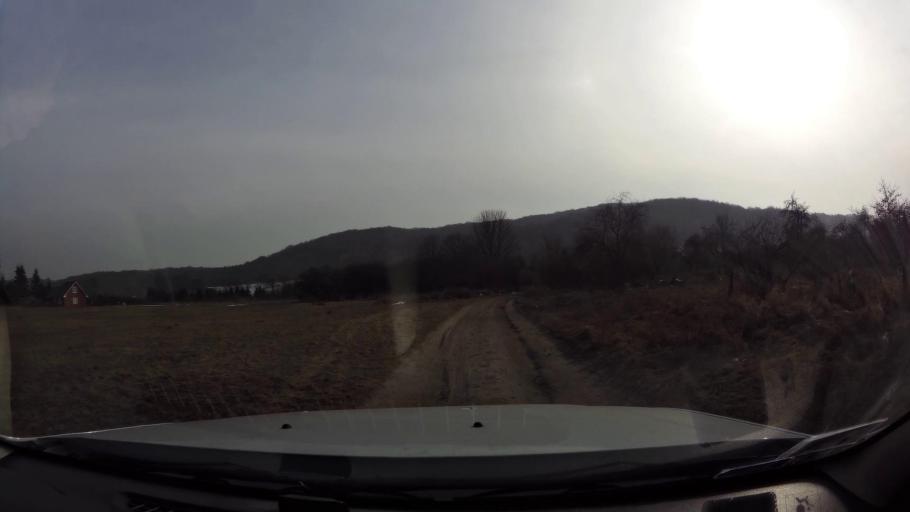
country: PL
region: West Pomeranian Voivodeship
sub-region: Powiat kamienski
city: Miedzyzdroje
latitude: 53.8811
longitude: 14.4481
